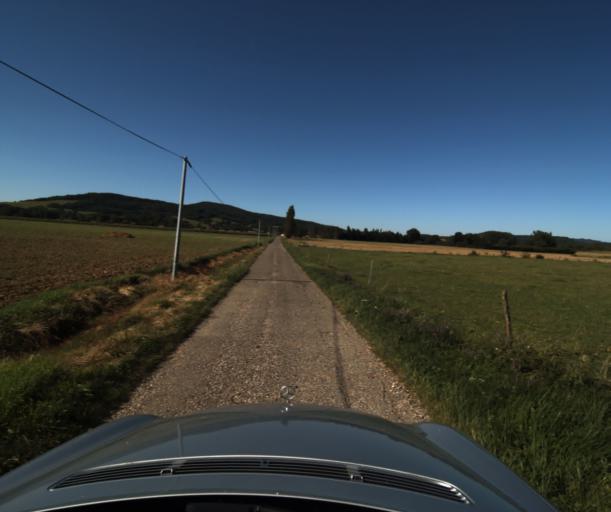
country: FR
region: Midi-Pyrenees
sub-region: Departement de l'Ariege
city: Lavelanet
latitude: 42.9811
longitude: 1.9029
